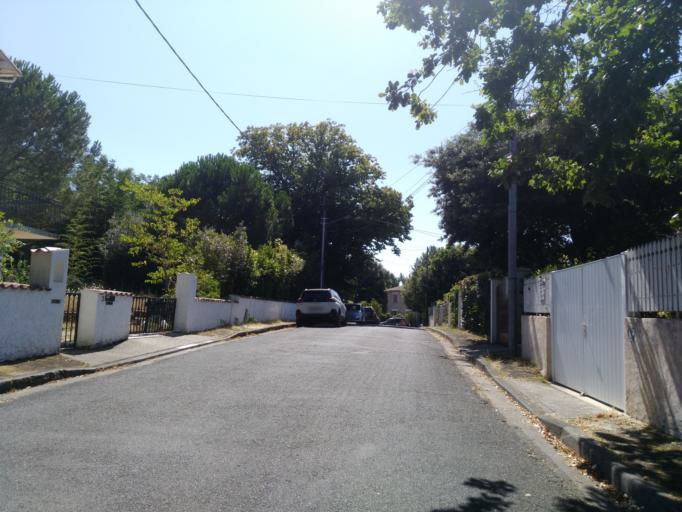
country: FR
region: Poitou-Charentes
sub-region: Departement de la Charente-Maritime
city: Saint-Palais-sur-Mer
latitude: 45.6426
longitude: -1.0819
